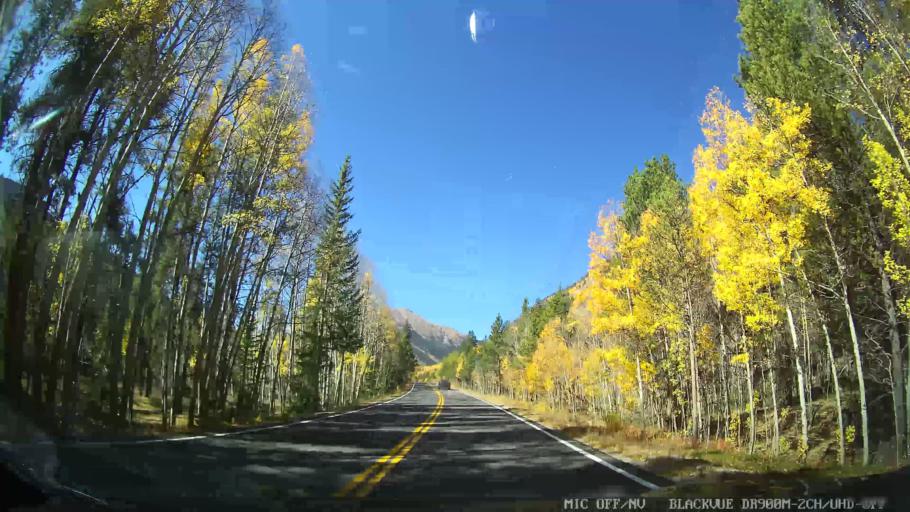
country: US
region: Colorado
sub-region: Lake County
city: Leadville North
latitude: 39.0717
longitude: -106.4791
